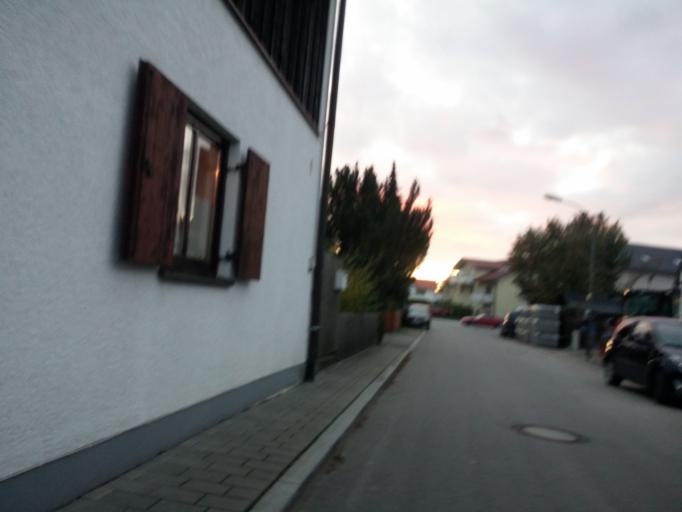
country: DE
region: Bavaria
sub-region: Upper Bavaria
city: Forstern
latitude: 48.1823
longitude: 11.9770
